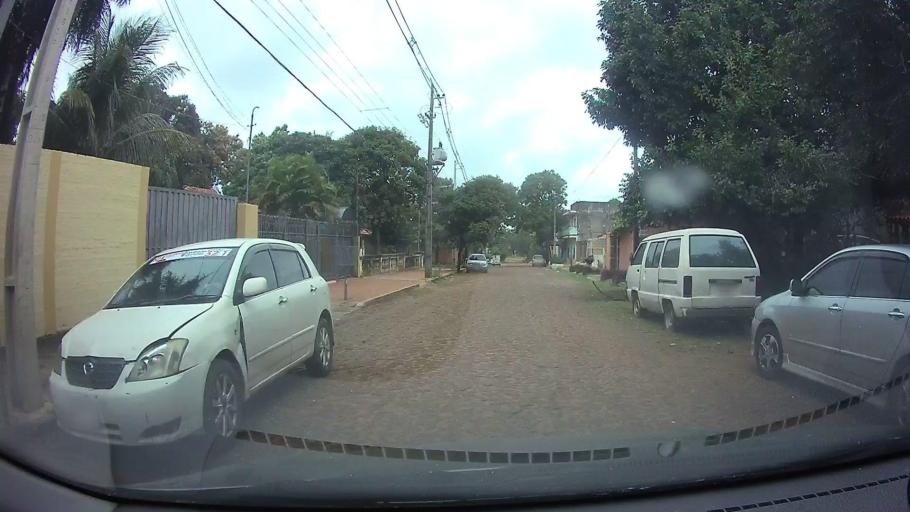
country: PY
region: Central
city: San Lorenzo
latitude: -25.3197
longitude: -57.5073
